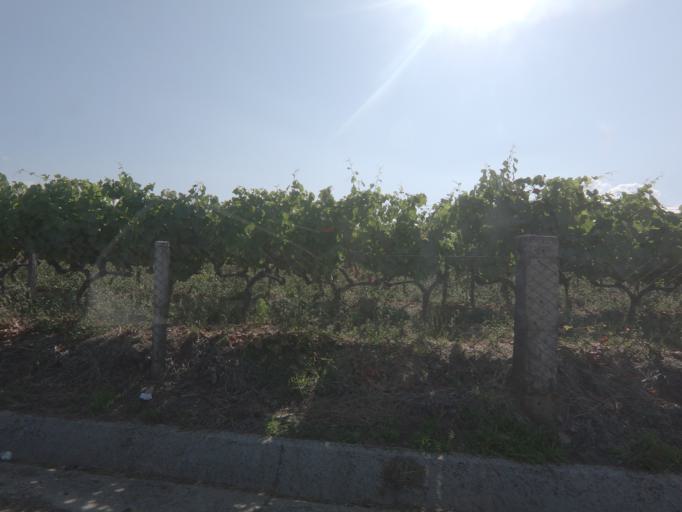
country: PT
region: Vila Real
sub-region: Sabrosa
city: Sabrosa
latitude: 41.2602
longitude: -7.5776
